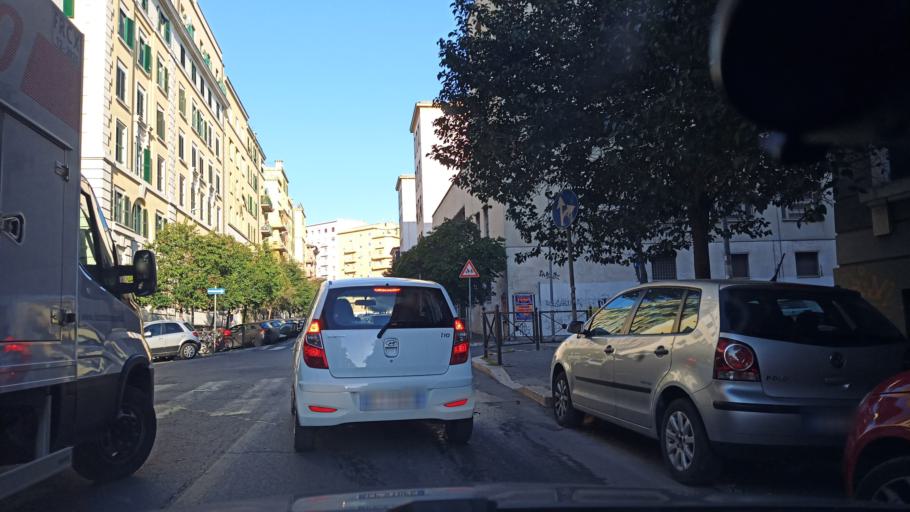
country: IT
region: Latium
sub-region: Citta metropolitana di Roma Capitale
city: Rome
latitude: 41.8804
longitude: 12.5120
